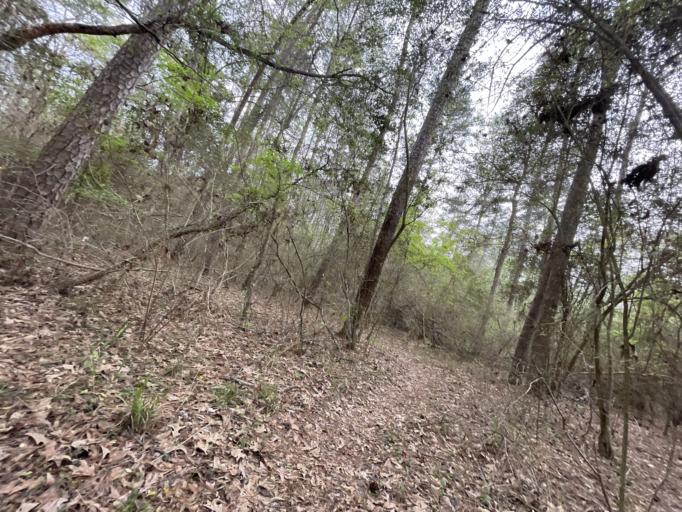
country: US
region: Texas
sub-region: Walker County
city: Huntsville
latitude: 30.6600
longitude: -95.4860
